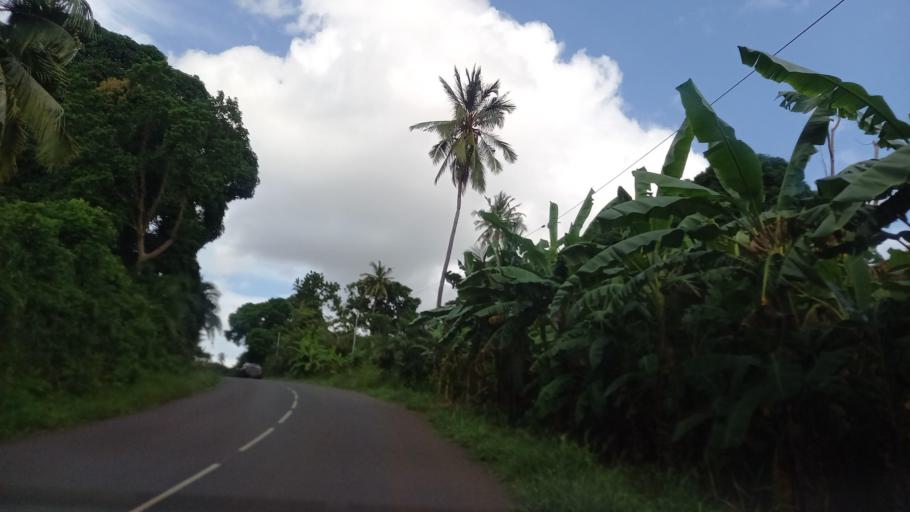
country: YT
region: Boueni
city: Boueni
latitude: -12.9188
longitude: 45.1015
